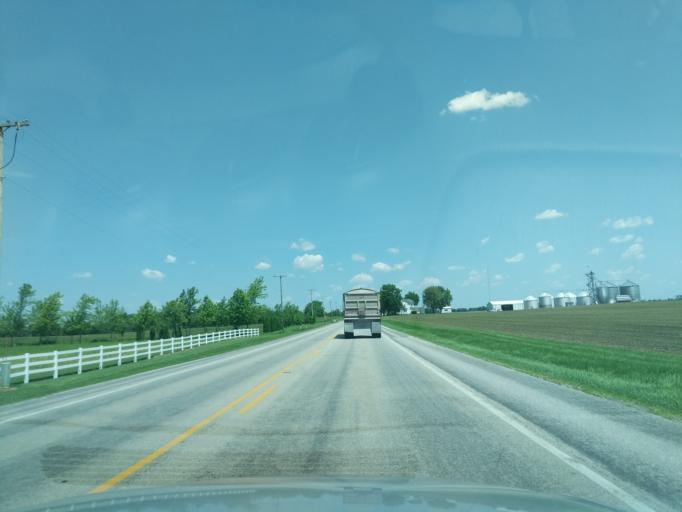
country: US
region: Indiana
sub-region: Noble County
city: Ligonier
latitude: 41.4889
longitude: -85.5775
